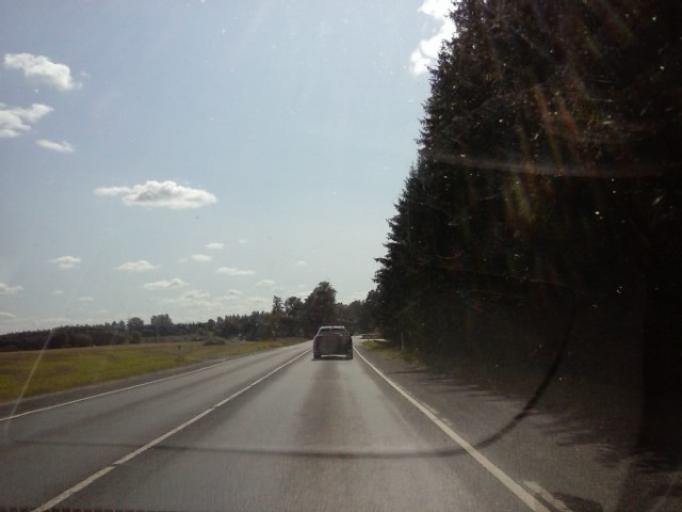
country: EE
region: Tartu
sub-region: UElenurme vald
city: Ulenurme
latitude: 58.2525
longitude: 26.7847
